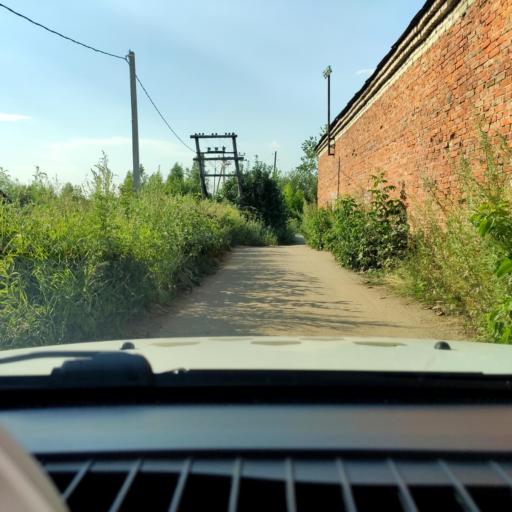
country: RU
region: Perm
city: Perm
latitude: 58.0284
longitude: 56.2384
